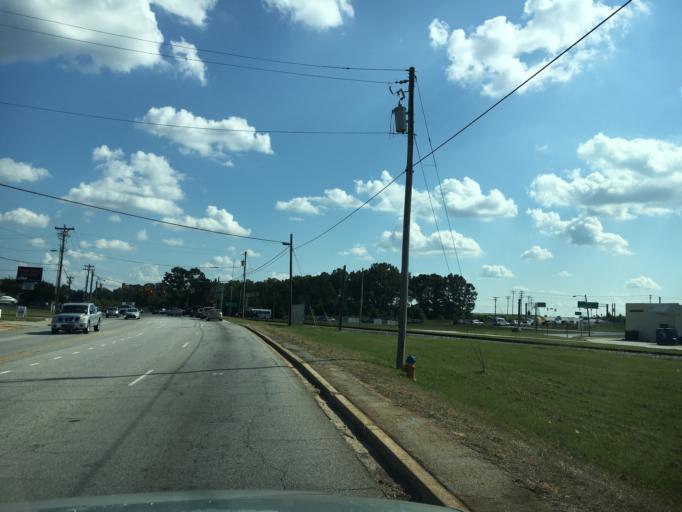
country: US
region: South Carolina
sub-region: Greenville County
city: Simpsonville
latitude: 34.7234
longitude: -82.2538
